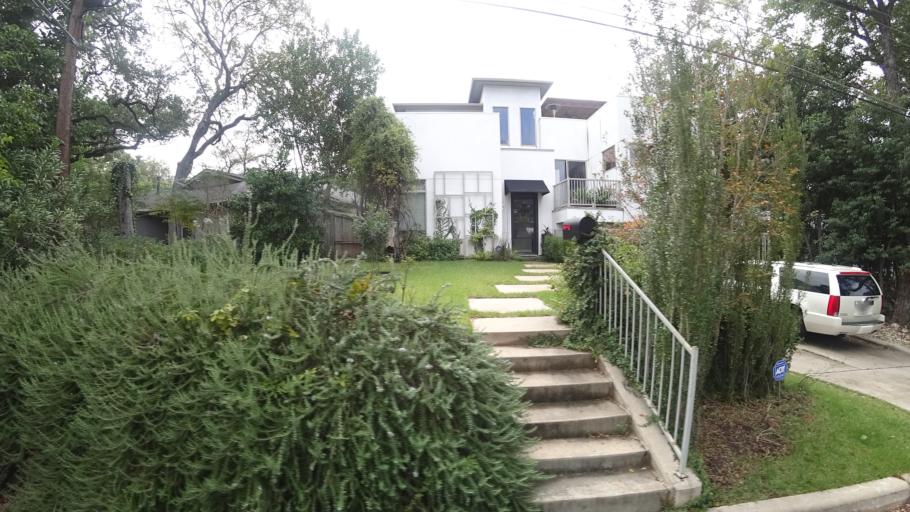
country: US
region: Texas
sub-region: Travis County
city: Austin
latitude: 30.2593
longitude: -97.7556
